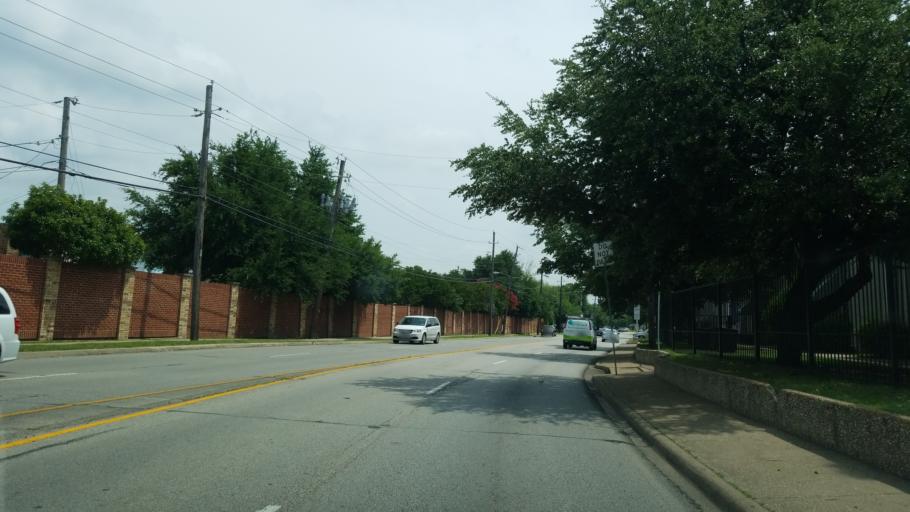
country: US
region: Texas
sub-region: Dallas County
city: Farmers Branch
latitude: 32.9082
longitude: -96.8808
